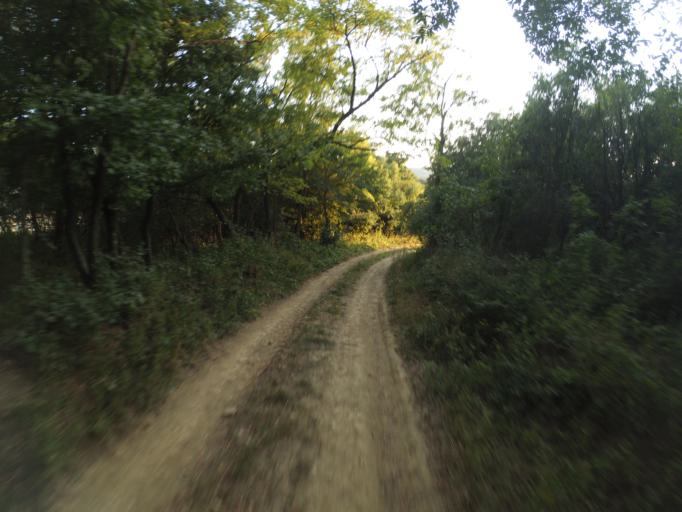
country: HU
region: Pest
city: Pilisszanto
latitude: 47.6703
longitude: 18.8739
